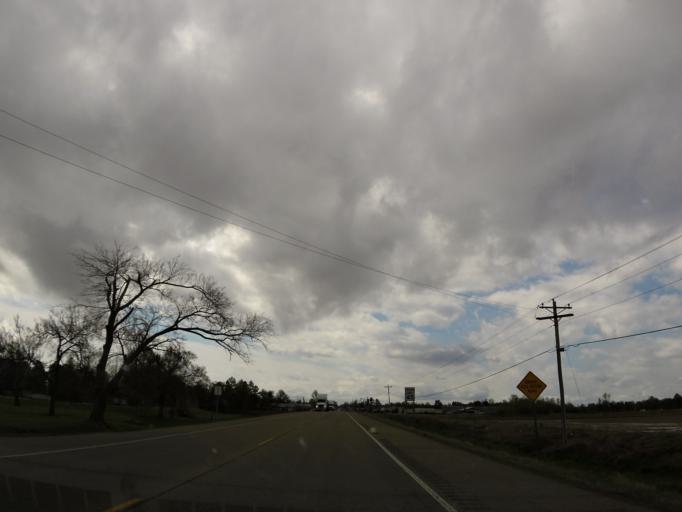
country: US
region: Arkansas
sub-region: Clay County
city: Corning
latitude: 36.4274
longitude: -90.5860
